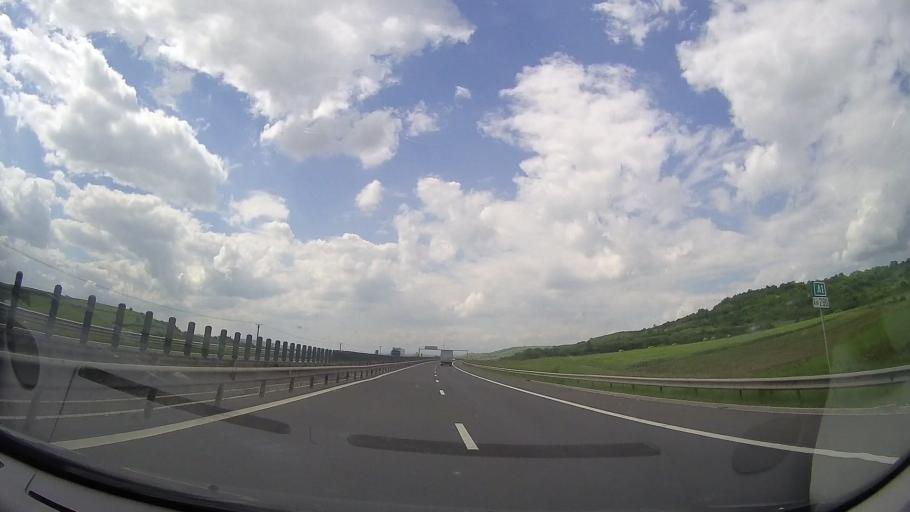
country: RO
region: Sibiu
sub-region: Comuna Apoldu de Jos
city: Apoldu de Jos
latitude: 45.8773
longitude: 23.8658
